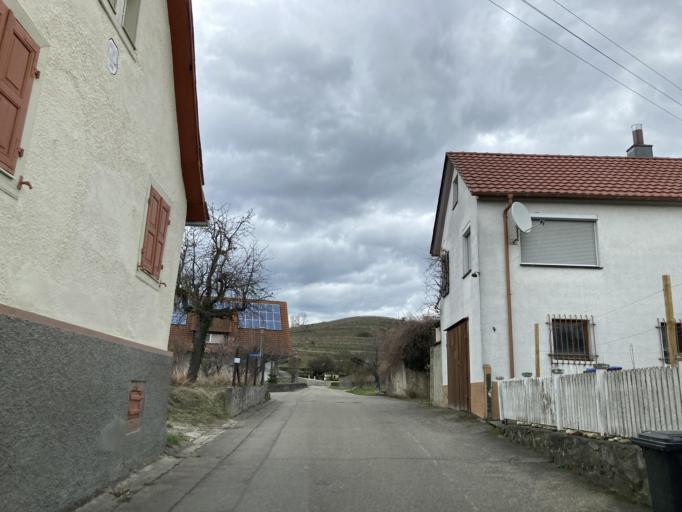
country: DE
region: Baden-Wuerttemberg
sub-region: Freiburg Region
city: Vogtsburg
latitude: 48.1050
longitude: 7.6295
